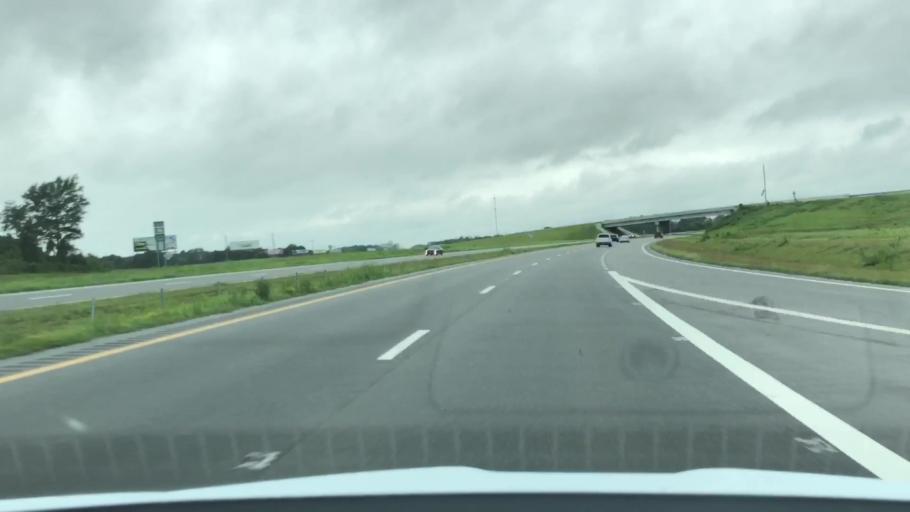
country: US
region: North Carolina
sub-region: Lenoir County
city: La Grange
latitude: 35.3016
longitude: -77.8164
